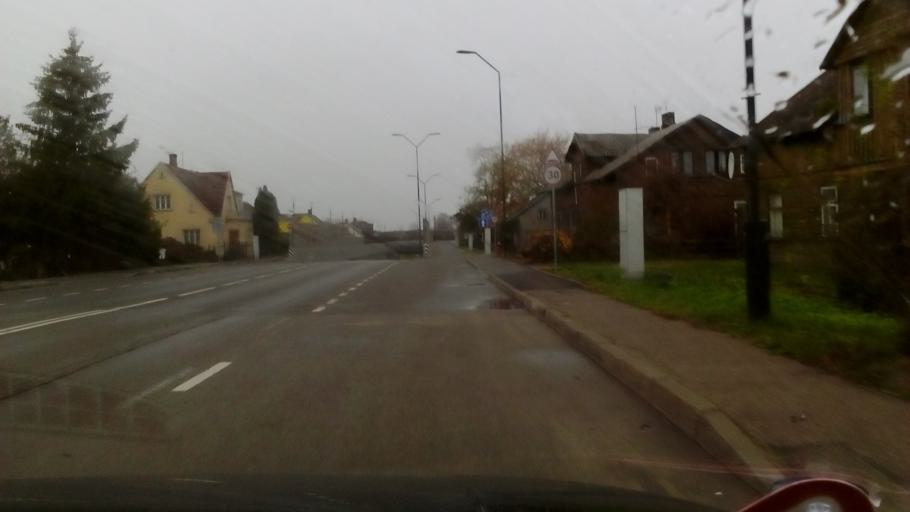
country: LT
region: Marijampoles apskritis
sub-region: Marijampole Municipality
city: Marijampole
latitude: 54.5546
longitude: 23.3678
